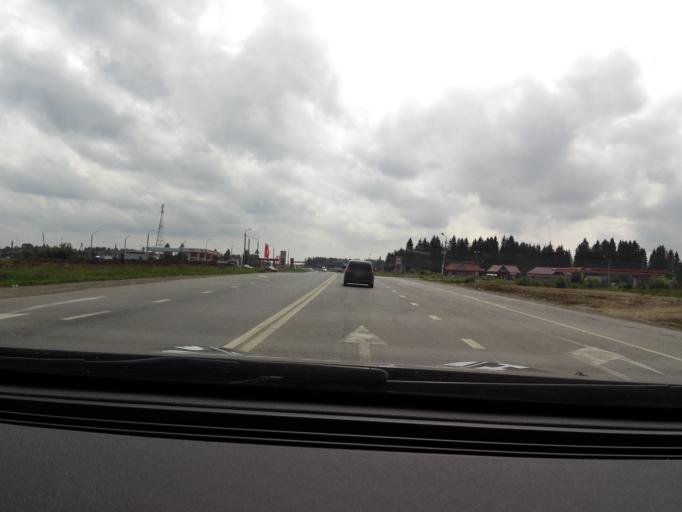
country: RU
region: Perm
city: Kukushtan
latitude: 57.6439
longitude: 56.4471
